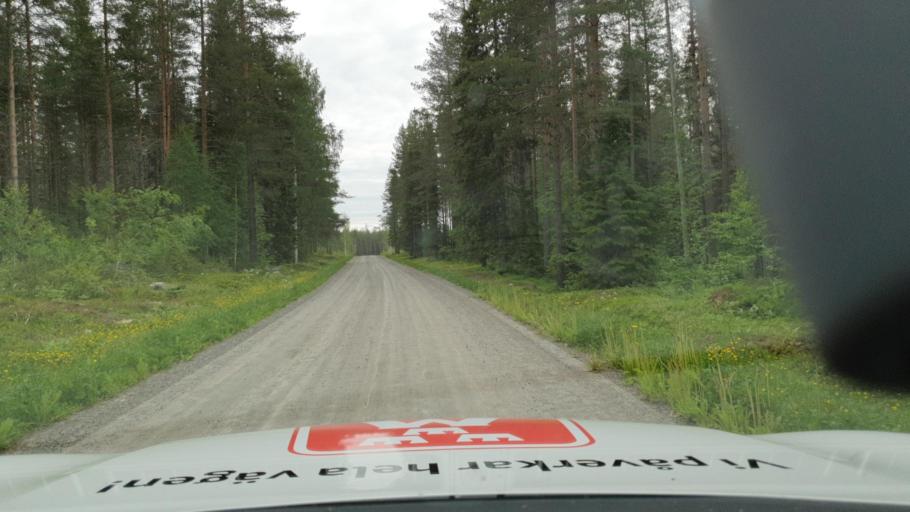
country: SE
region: Vaesterbotten
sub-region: Skelleftea Kommun
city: Langsele
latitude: 64.4772
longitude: 20.2088
